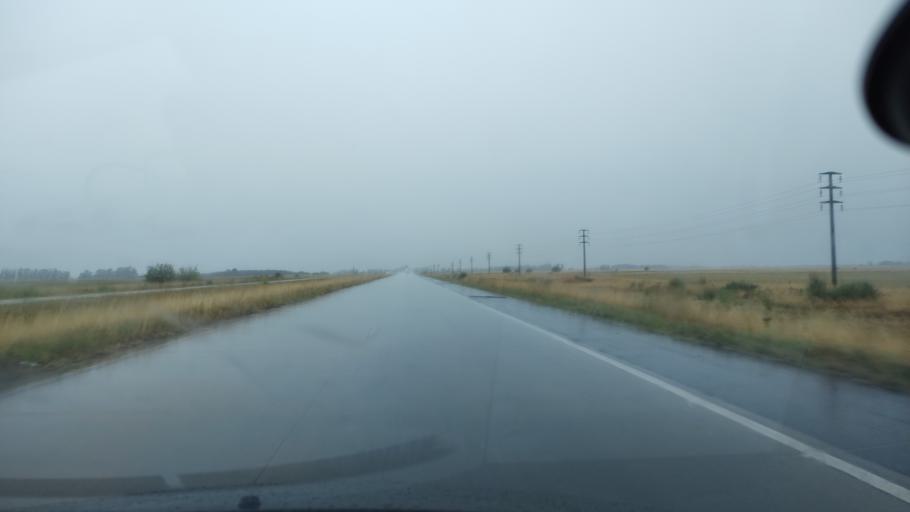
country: AR
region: Buenos Aires
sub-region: Partido de San Vicente
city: San Vicente
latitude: -35.0737
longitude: -58.5406
